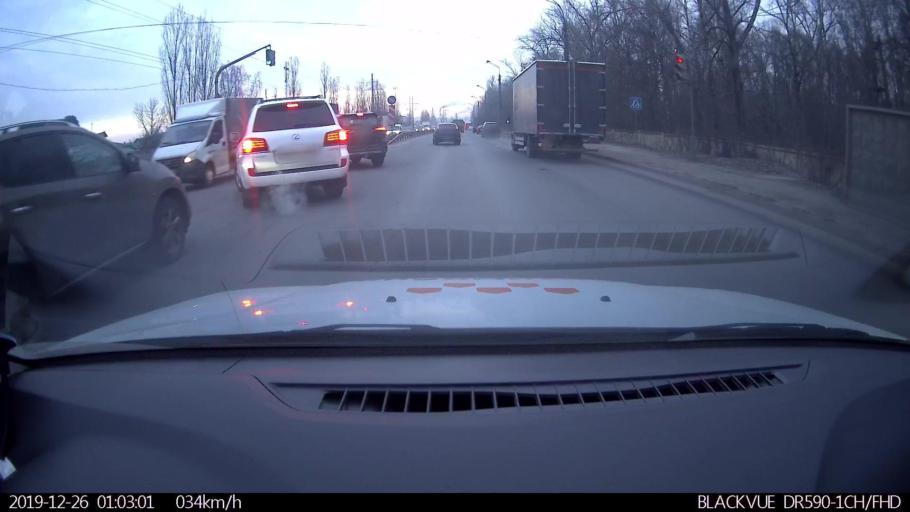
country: RU
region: Nizjnij Novgorod
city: Nizhniy Novgorod
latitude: 56.2885
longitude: 43.8878
